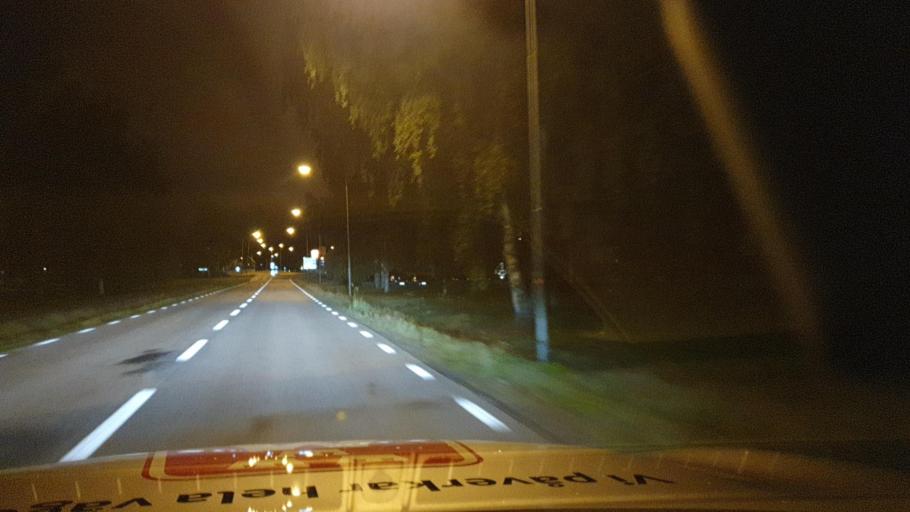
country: SE
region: Vaesternorrland
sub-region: Solleftea Kommun
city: Solleftea
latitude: 63.1778
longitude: 17.2813
